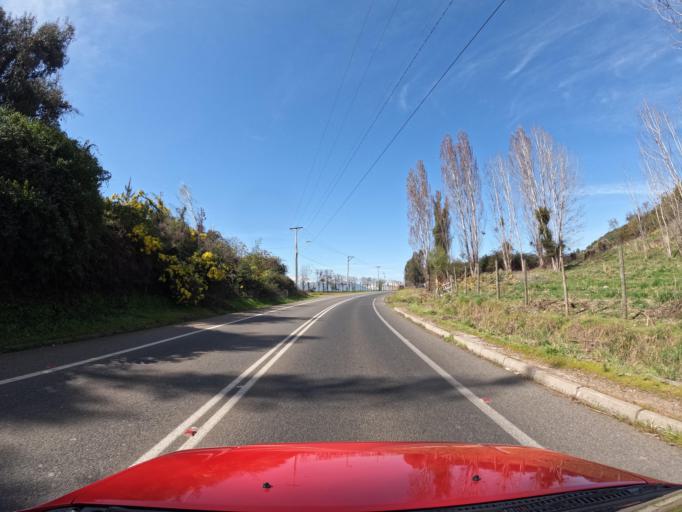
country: CL
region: Maule
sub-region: Provincia de Curico
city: Teno
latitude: -34.9776
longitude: -70.9661
